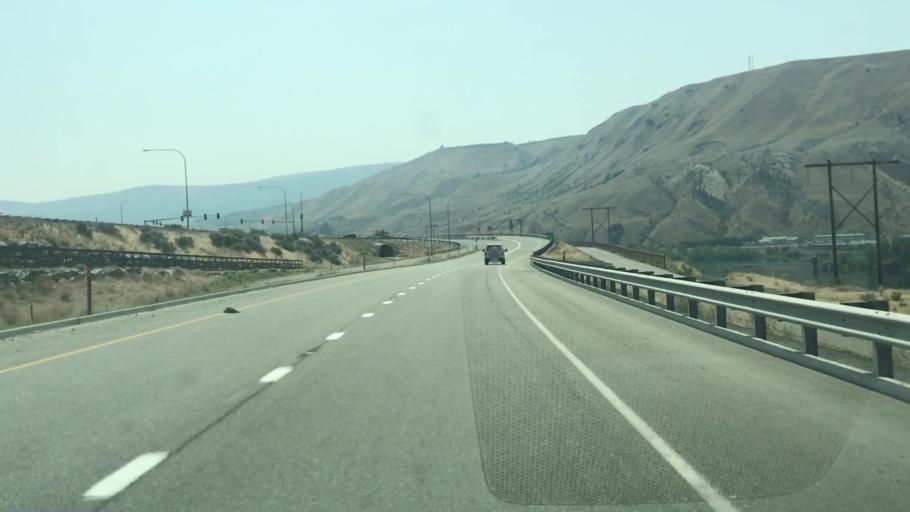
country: US
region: Washington
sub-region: Chelan County
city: South Wenatchee
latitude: 47.4012
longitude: -120.2892
